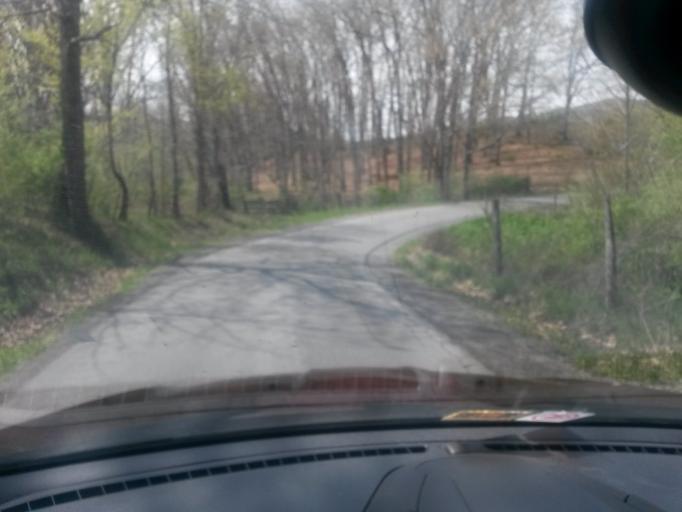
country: US
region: West Virginia
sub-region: Pocahontas County
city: Marlinton
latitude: 38.0827
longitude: -80.2273
